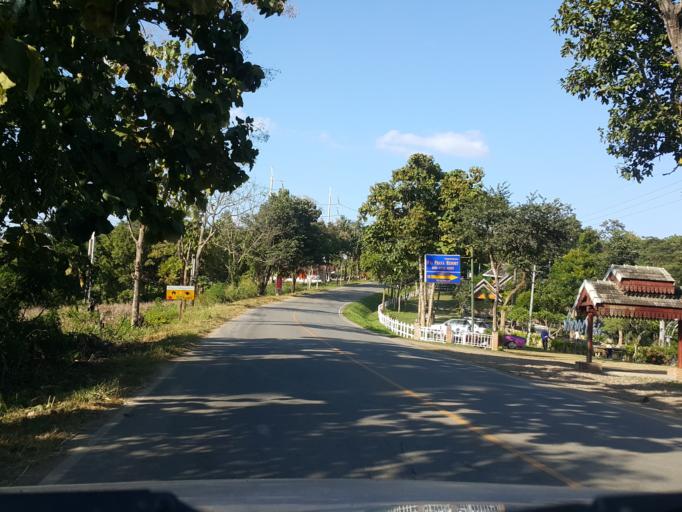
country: TH
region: Mae Hong Son
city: Mae Hi
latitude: 19.3356
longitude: 98.4317
